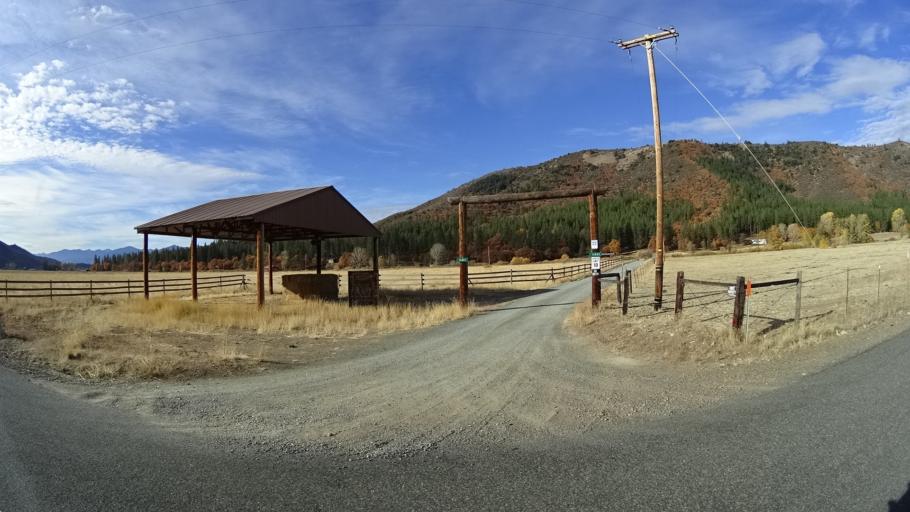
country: US
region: California
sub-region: Siskiyou County
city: Yreka
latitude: 41.6453
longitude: -122.8294
